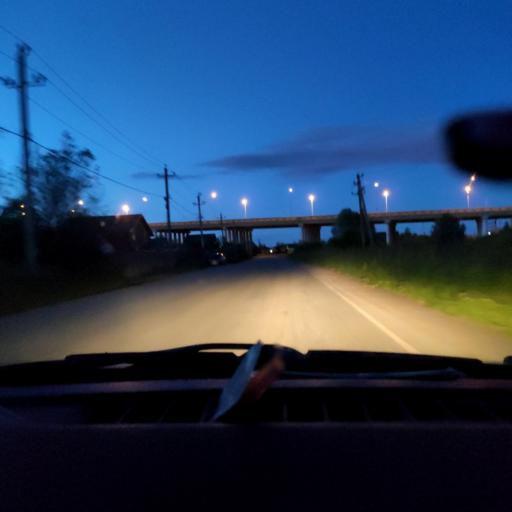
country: RU
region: Perm
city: Kondratovo
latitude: 58.0128
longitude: 56.0488
